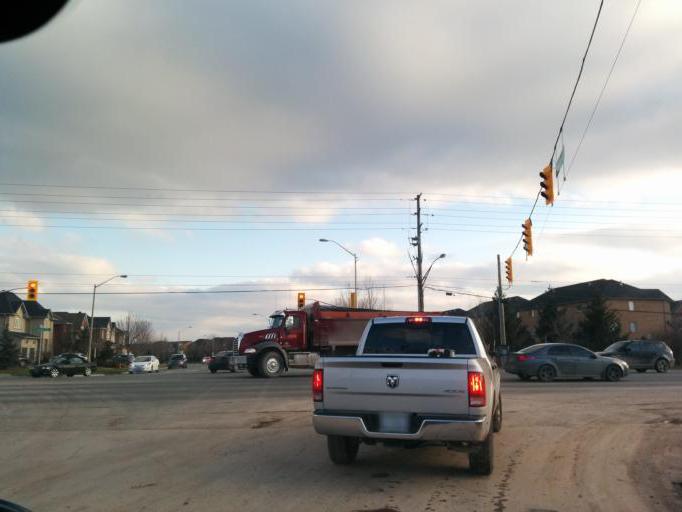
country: CA
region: Ontario
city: Oakville
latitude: 43.4696
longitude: -79.7401
